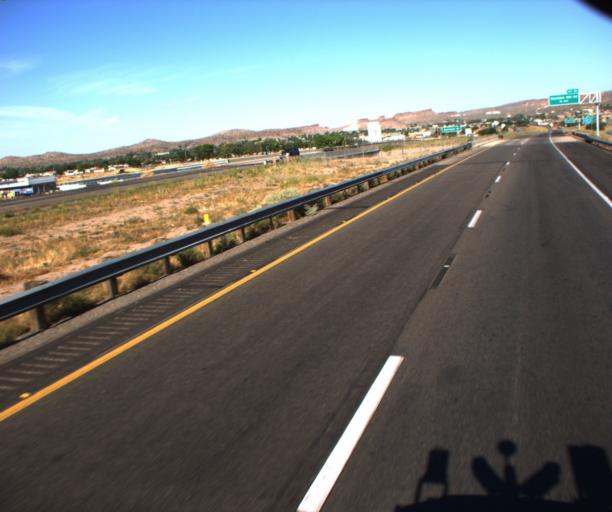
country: US
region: Arizona
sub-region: Mohave County
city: Kingman
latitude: 35.2172
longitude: -114.0237
